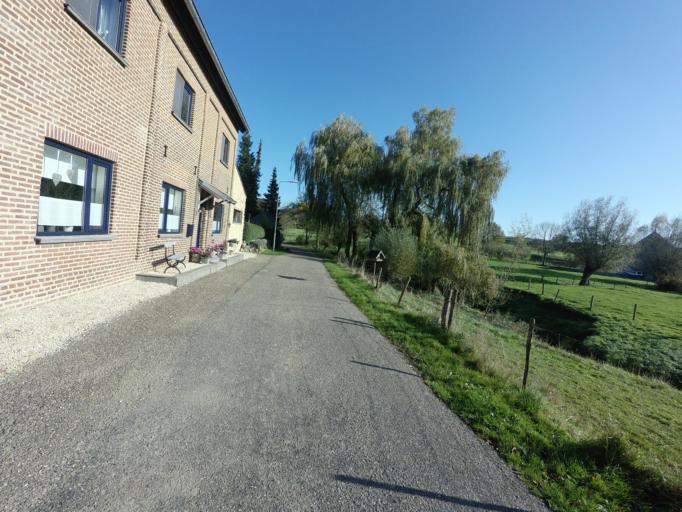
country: NL
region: Limburg
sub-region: Gemeente Simpelveld
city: Simpelveld
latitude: 50.8305
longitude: 5.9642
